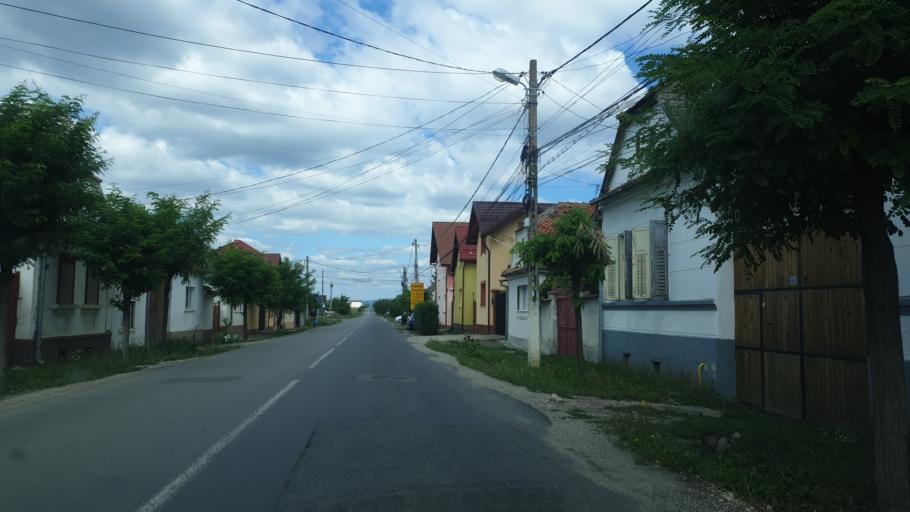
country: RO
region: Brasov
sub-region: Comuna Sanpetru
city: Sanpetru
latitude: 45.7185
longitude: 25.6275
